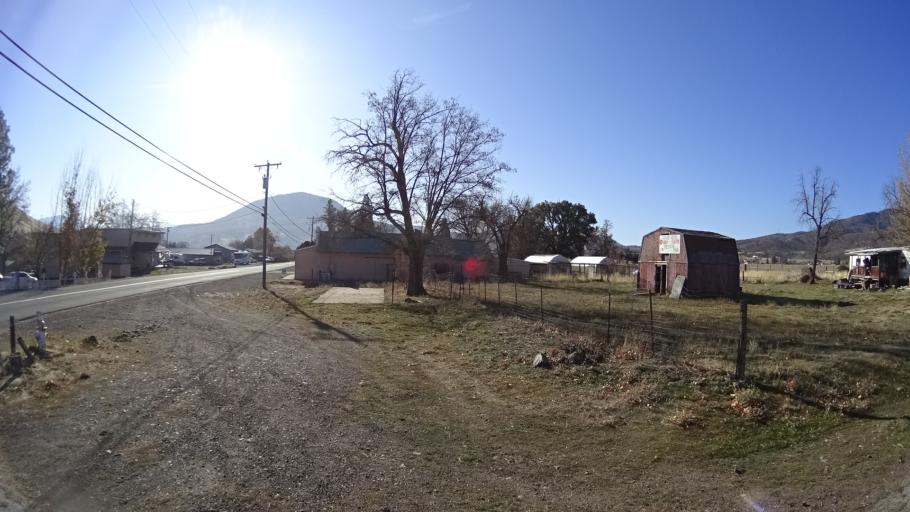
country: US
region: California
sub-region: Siskiyou County
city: Montague
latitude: 41.9090
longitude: -122.5587
